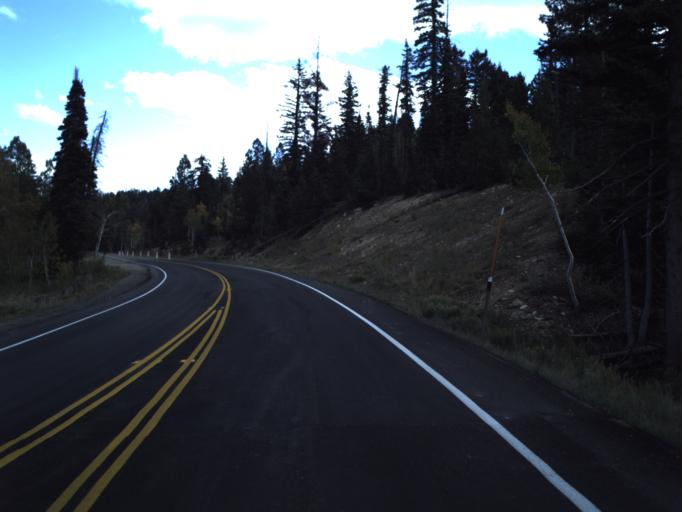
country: US
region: Utah
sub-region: Iron County
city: Parowan
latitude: 37.5153
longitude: -112.6969
